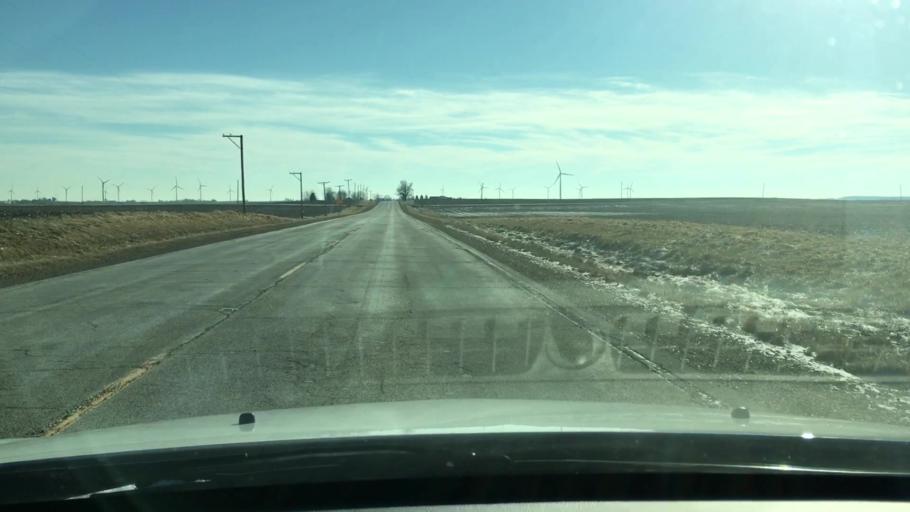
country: US
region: Illinois
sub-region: LaSalle County
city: Mendota
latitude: 41.6744
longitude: -89.1297
